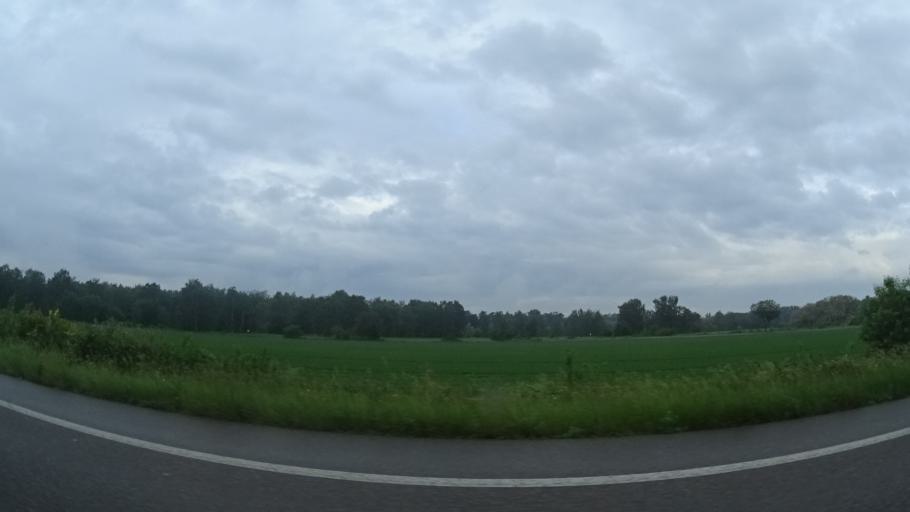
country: DE
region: Rheinland-Pfalz
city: Germersheim
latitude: 49.2100
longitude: 8.3500
